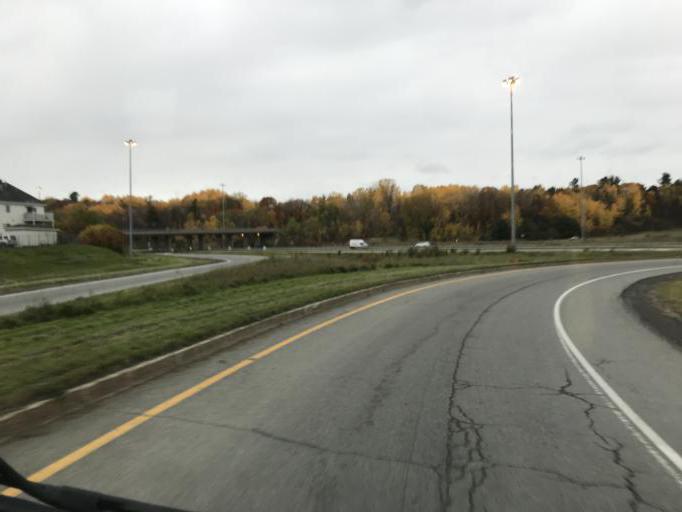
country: CA
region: Quebec
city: Bois-des-Filion
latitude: 45.6702
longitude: -73.7660
